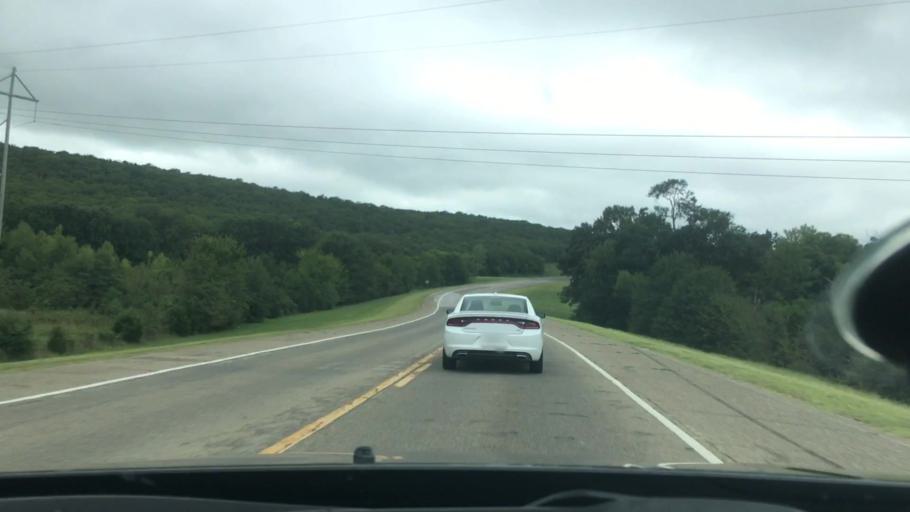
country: US
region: Oklahoma
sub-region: Sequoyah County
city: Vian
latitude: 35.5150
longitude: -94.9705
